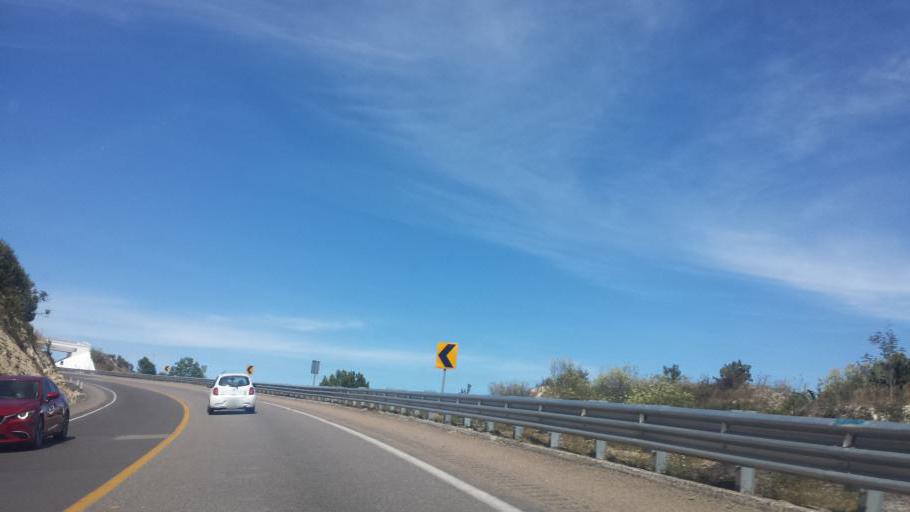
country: MX
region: Oaxaca
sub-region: Villa Tejupam de la Union
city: Villa Tejupam de la Union
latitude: 17.6556
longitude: -97.3396
